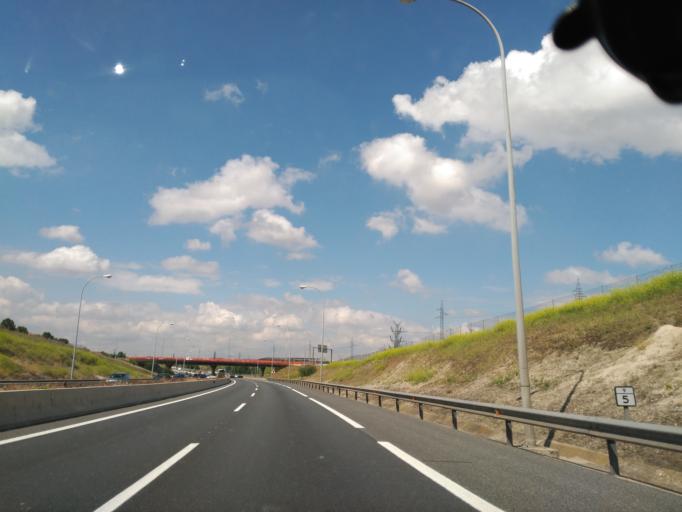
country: ES
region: Madrid
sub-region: Provincia de Madrid
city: Villaverde
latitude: 40.3371
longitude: -3.6750
